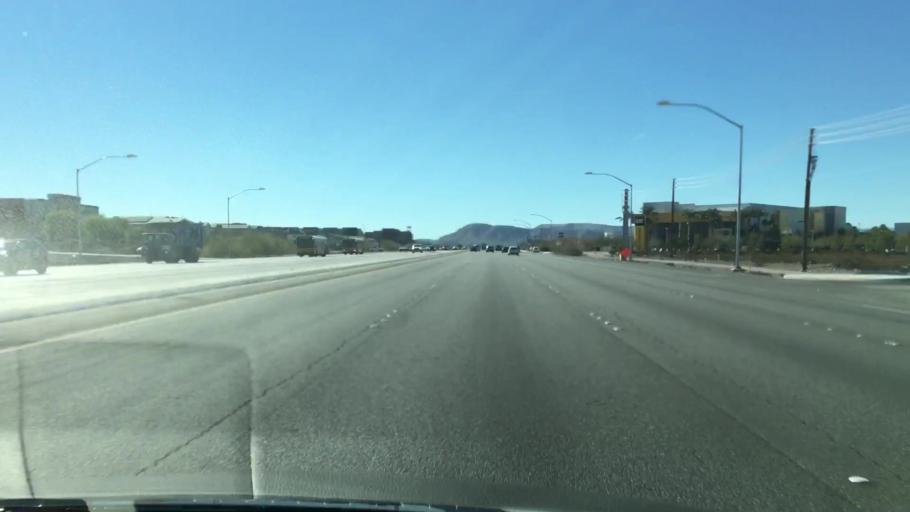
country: US
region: Nevada
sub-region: Clark County
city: Whitney
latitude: 35.9982
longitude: -115.1272
